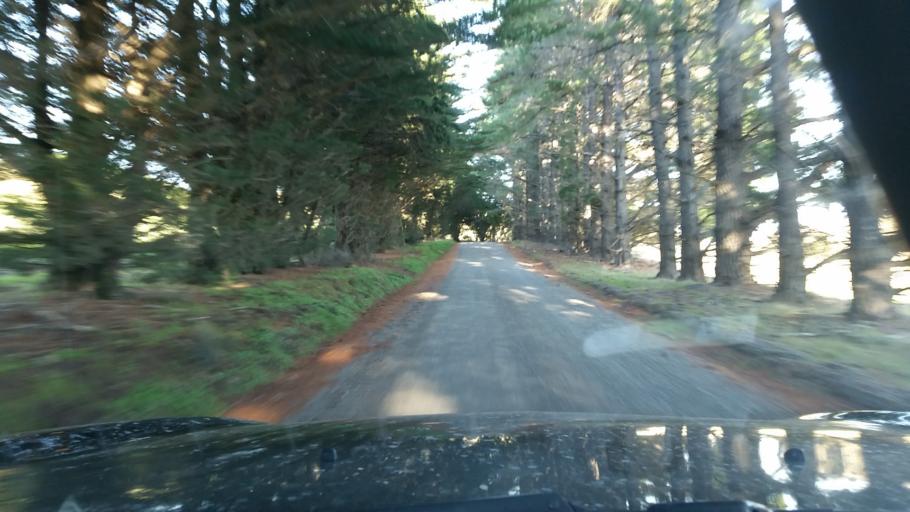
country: NZ
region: Marlborough
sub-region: Marlborough District
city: Blenheim
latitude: -41.7343
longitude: 174.0001
